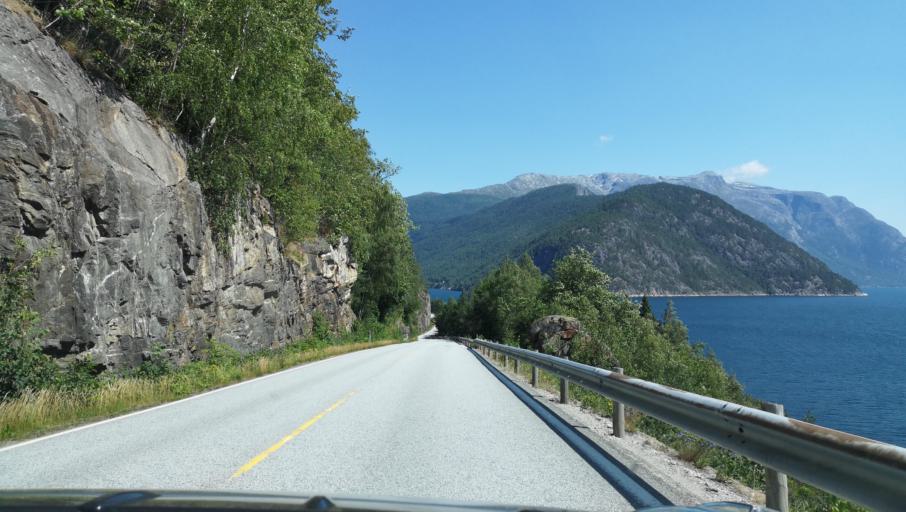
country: NO
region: Hordaland
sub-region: Ulvik
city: Ulvik
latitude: 60.4878
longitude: 6.8845
